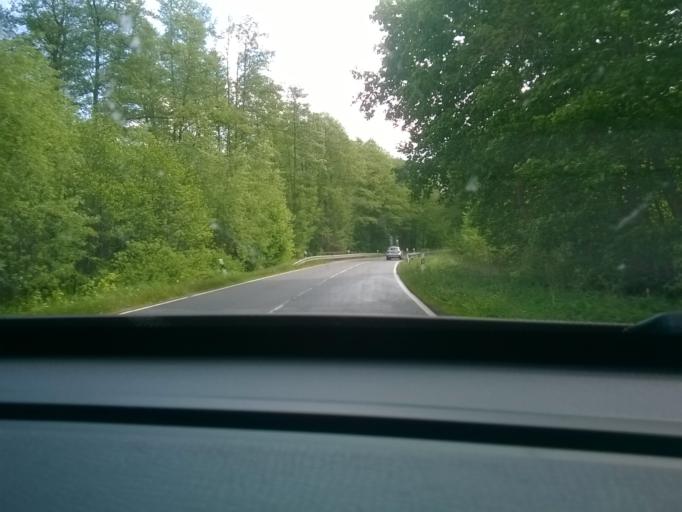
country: DE
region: Brandenburg
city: Wittstock
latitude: 53.0698
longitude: 12.5509
